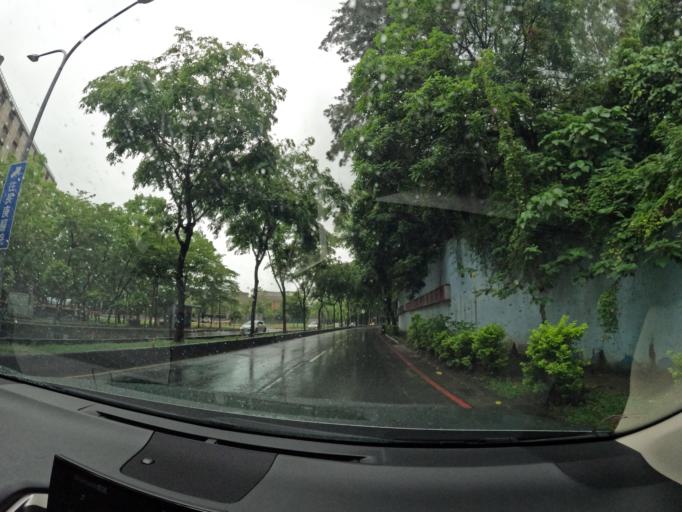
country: TW
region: Taiwan
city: Fengshan
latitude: 22.6506
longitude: 120.3534
